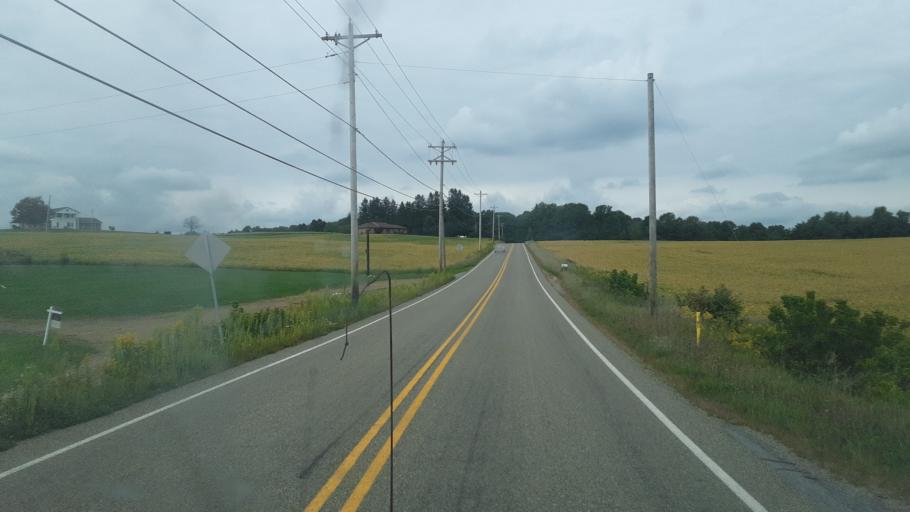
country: US
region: Pennsylvania
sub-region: Jefferson County
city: Punxsutawney
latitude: 40.9661
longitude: -79.0989
